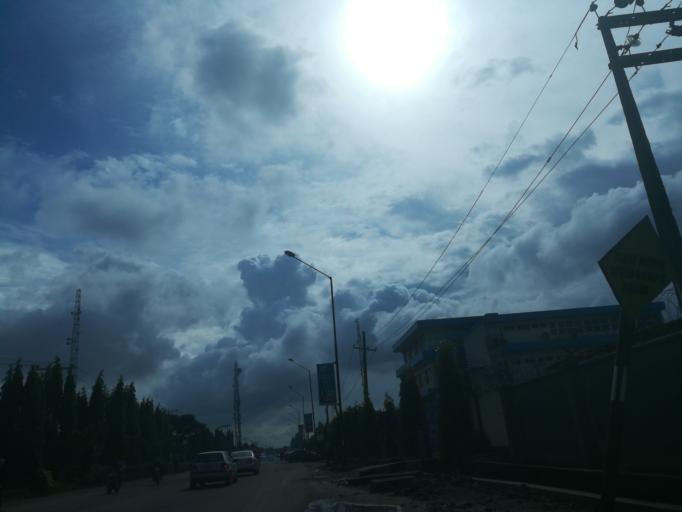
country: NG
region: Lagos
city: Agege
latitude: 6.6238
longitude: 3.3407
